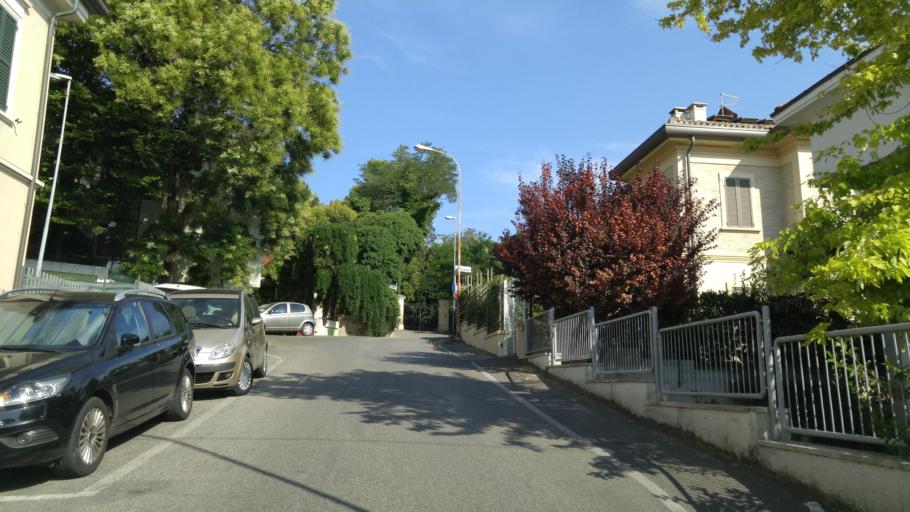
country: IT
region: The Marches
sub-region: Provincia di Pesaro e Urbino
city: Pesaro
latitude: 43.9049
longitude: 12.9224
